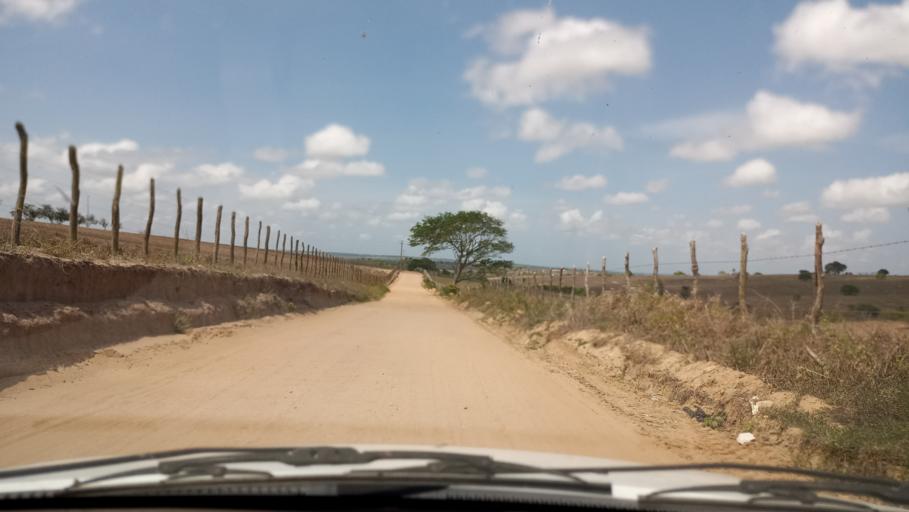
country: BR
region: Rio Grande do Norte
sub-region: Goianinha
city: Goianinha
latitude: -6.3456
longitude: -35.3291
